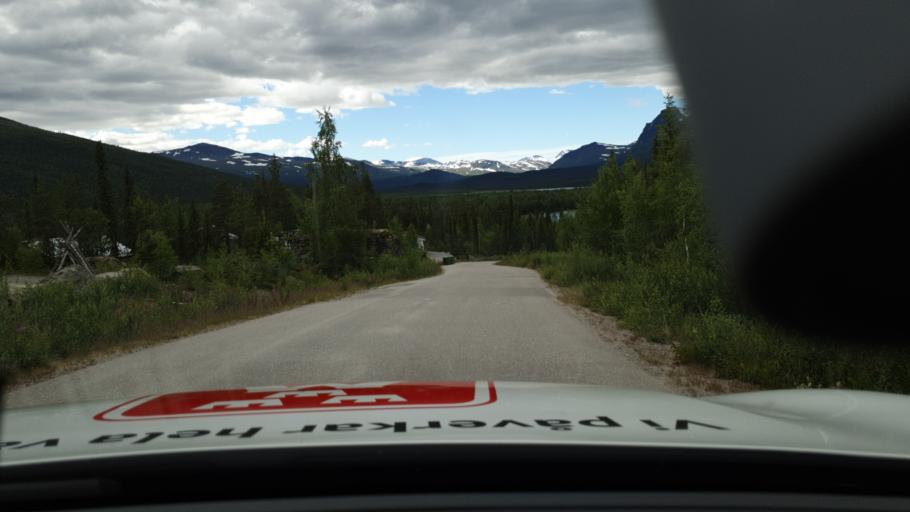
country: SE
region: Norrbotten
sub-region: Arjeplogs Kommun
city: Arjeplog
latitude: 66.9462
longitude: 17.7334
